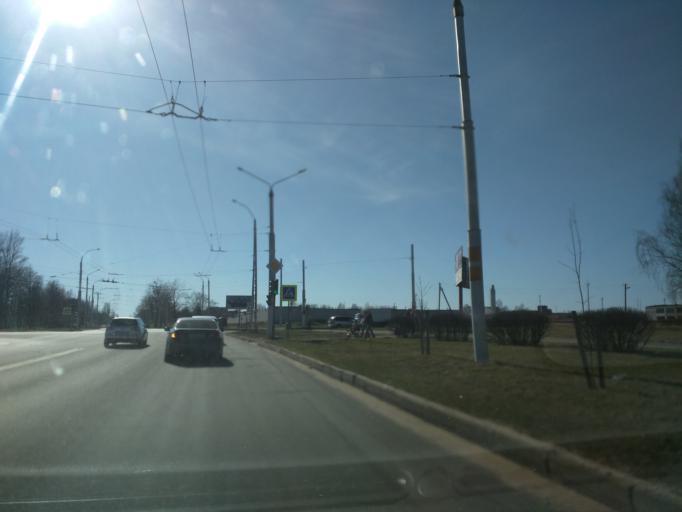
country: BY
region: Mogilev
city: Babruysk
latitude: 53.1841
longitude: 29.2161
